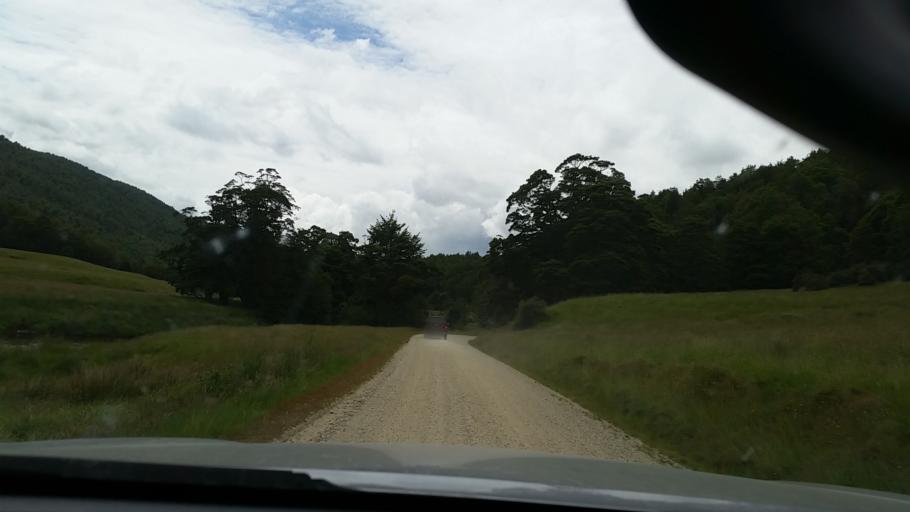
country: NZ
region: Otago
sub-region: Queenstown-Lakes District
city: Kingston
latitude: -45.5657
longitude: 169.0128
